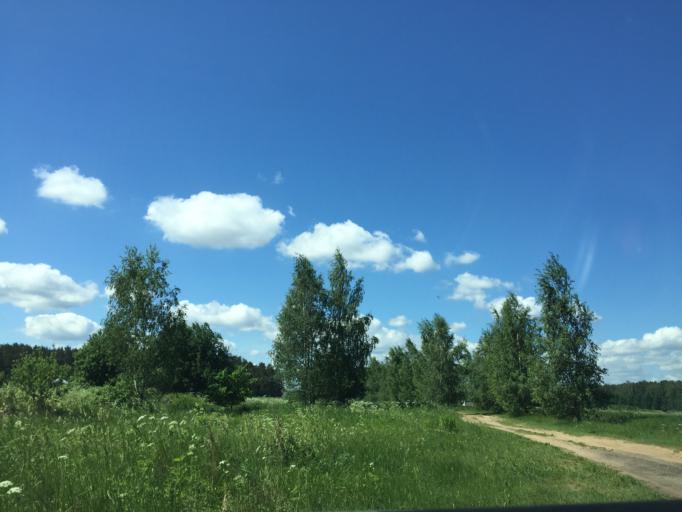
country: LV
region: Marupe
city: Marupe
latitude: 56.8857
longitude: 23.9747
